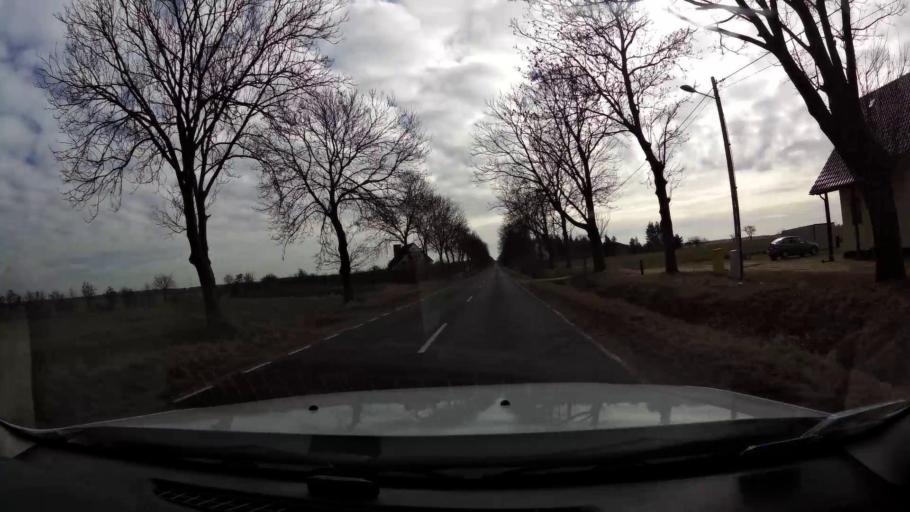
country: PL
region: West Pomeranian Voivodeship
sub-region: Powiat mysliborski
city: Debno
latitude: 52.7801
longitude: 14.6474
